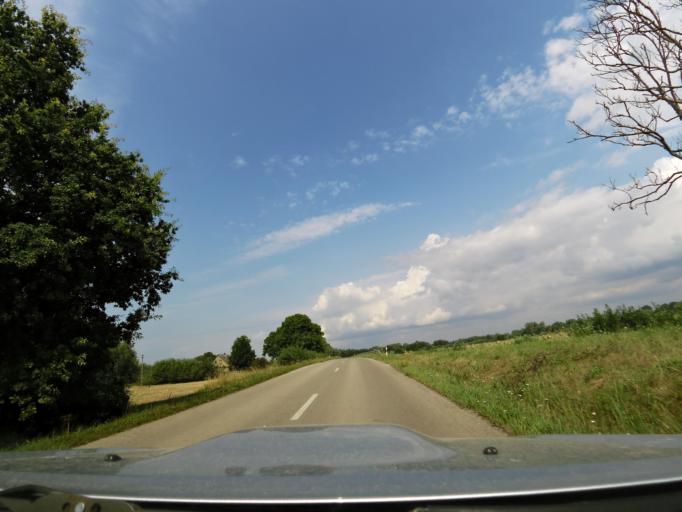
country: LT
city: Rusne
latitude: 55.3191
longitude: 21.3814
